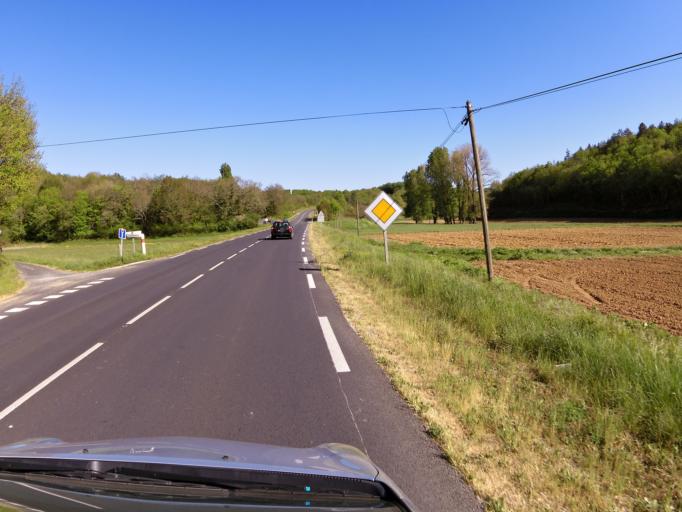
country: FR
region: Aquitaine
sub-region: Departement de la Dordogne
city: Montignac
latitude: 45.0533
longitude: 1.2078
